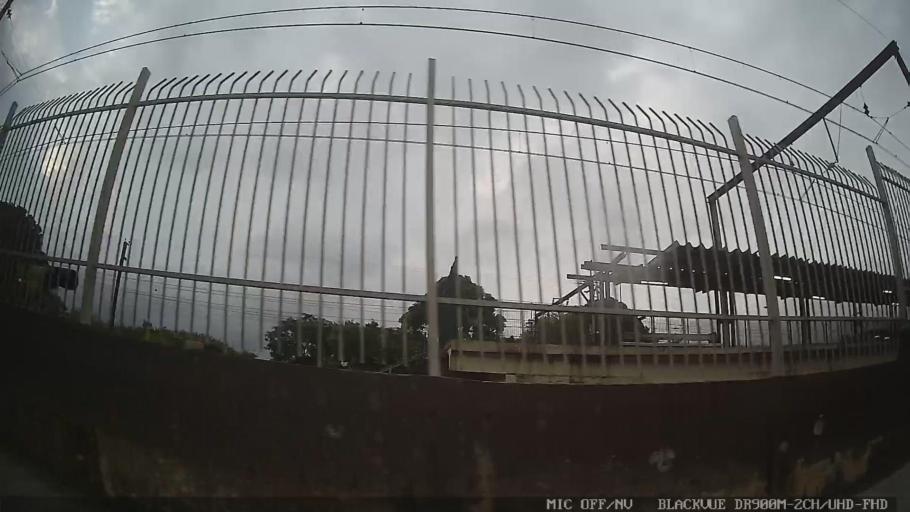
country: BR
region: Sao Paulo
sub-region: Mogi das Cruzes
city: Mogi das Cruzes
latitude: -23.5225
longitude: -46.1992
